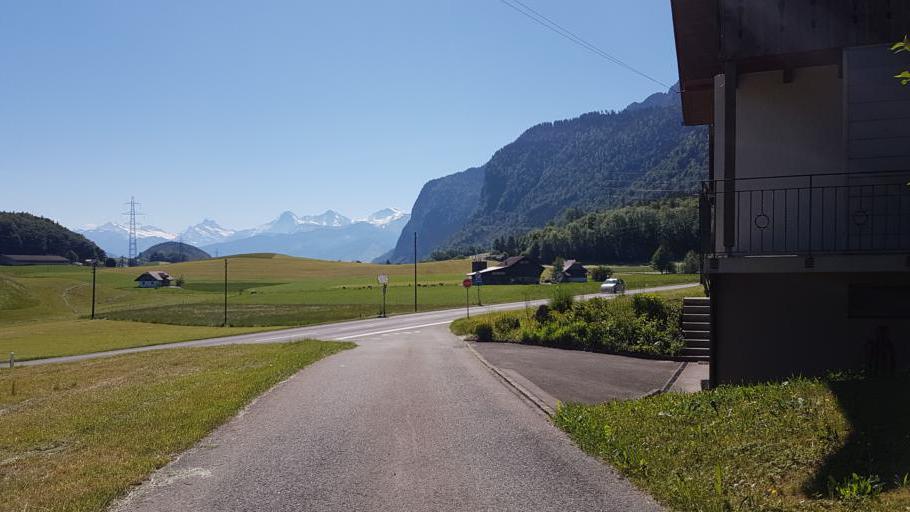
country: CH
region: Bern
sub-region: Thun District
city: Blumenstein
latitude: 46.7220
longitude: 7.5414
